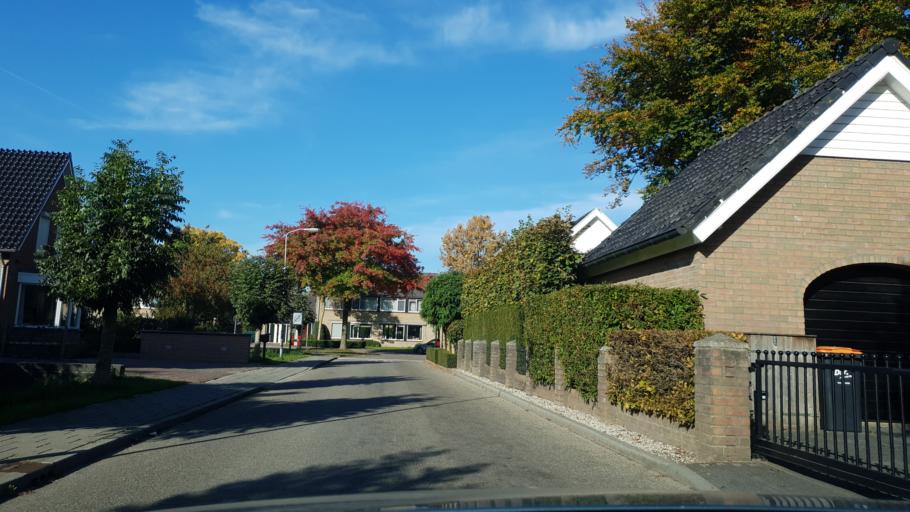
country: NL
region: Gelderland
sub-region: Gemeente Beuningen
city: Beuningen
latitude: 51.8581
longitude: 5.7812
